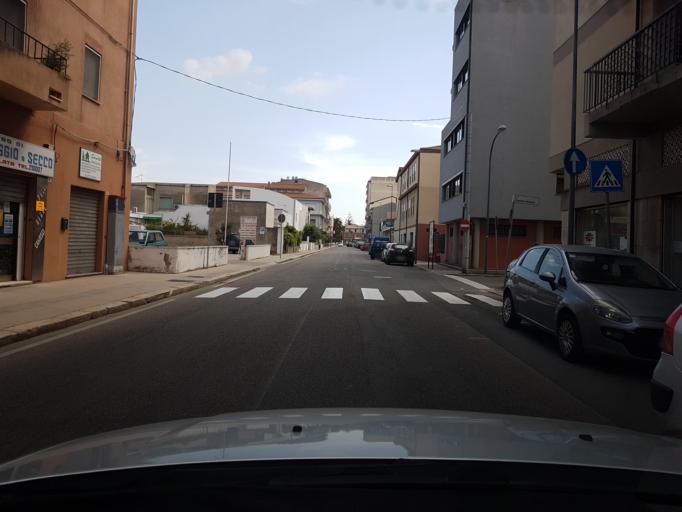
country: IT
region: Sardinia
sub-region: Provincia di Oristano
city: Oristano
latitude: 39.9085
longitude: 8.5926
